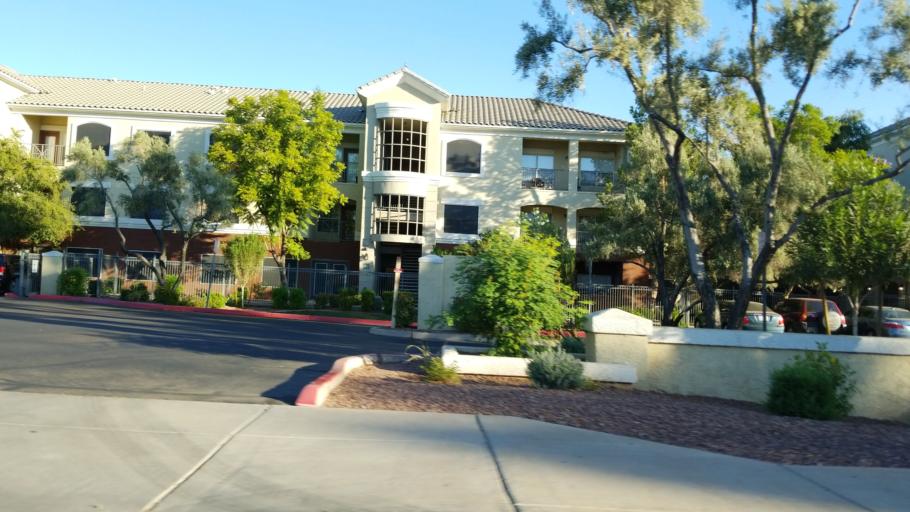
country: US
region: Arizona
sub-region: Maricopa County
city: Phoenix
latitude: 33.5314
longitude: -112.0974
